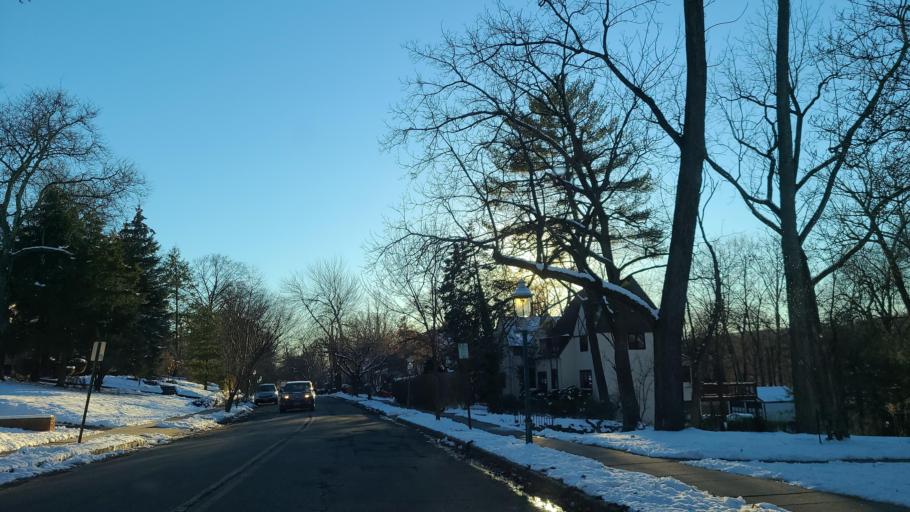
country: US
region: New Jersey
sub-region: Essex County
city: South Orange
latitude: 40.7520
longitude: -74.2547
